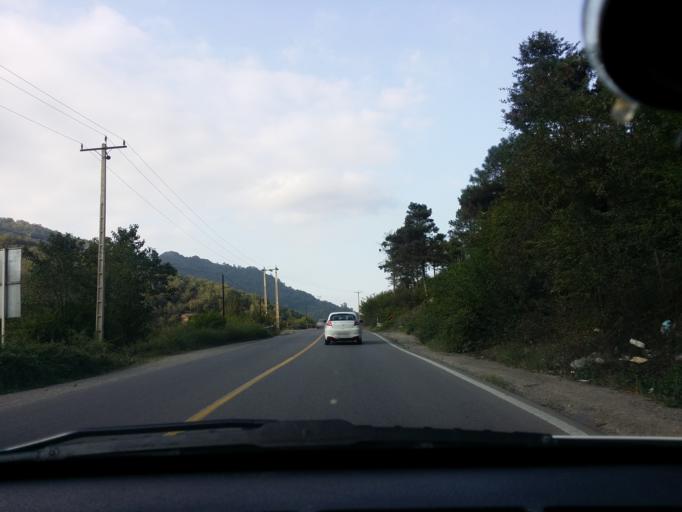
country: IR
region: Mazandaran
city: Chalus
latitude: 36.5563
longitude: 51.3724
